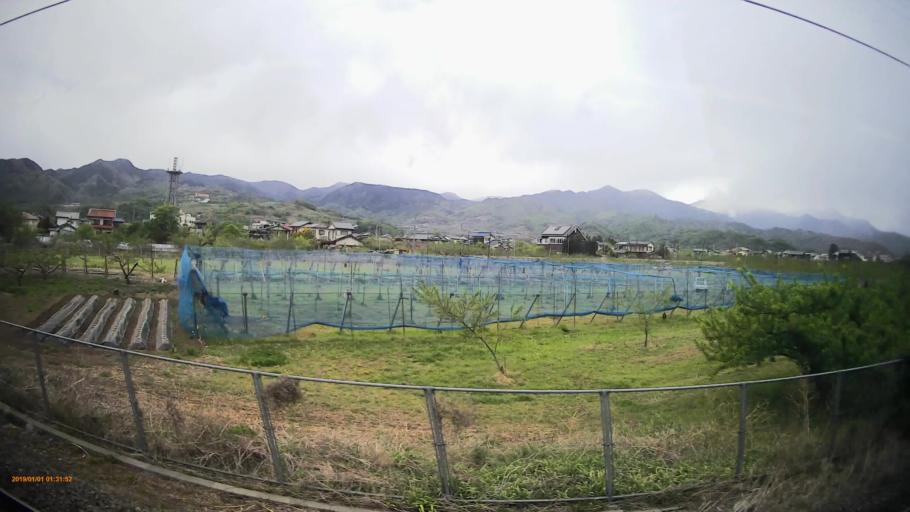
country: JP
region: Yamanashi
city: Enzan
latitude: 35.6893
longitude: 138.6938
